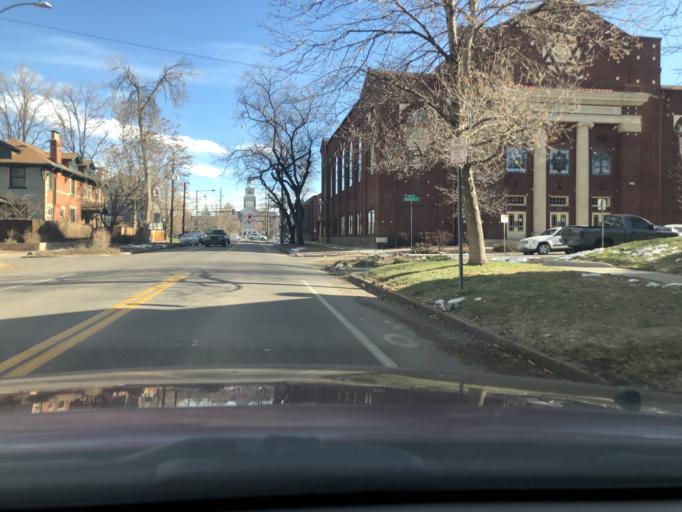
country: US
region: Colorado
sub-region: Denver County
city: Denver
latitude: 39.7416
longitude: -104.9614
